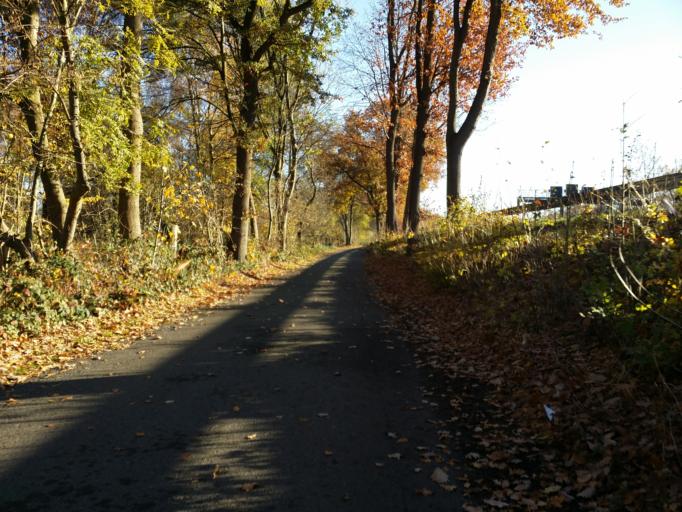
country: DE
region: Lower Saxony
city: Lilienthal
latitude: 53.0784
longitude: 8.9481
